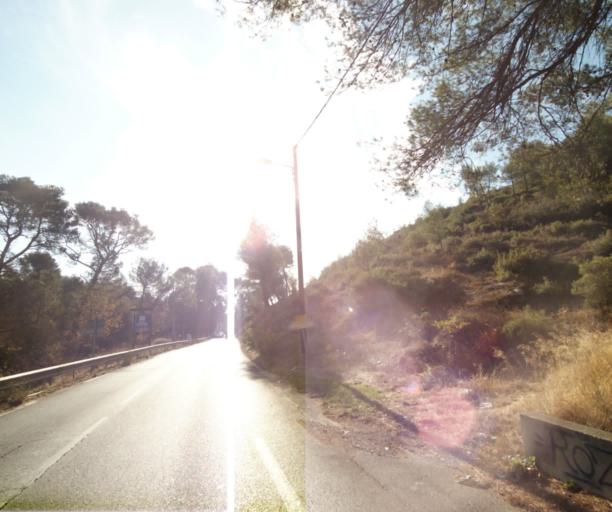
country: FR
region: Provence-Alpes-Cote d'Azur
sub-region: Departement des Bouches-du-Rhone
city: Allauch
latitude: 43.3154
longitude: 5.4975
